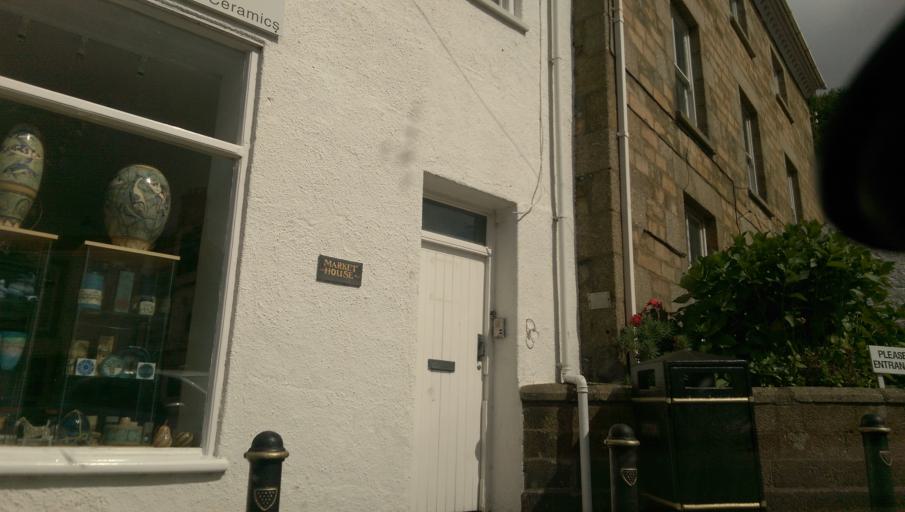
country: GB
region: England
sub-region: Cornwall
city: Marazion
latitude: 50.1237
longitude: -5.4723
